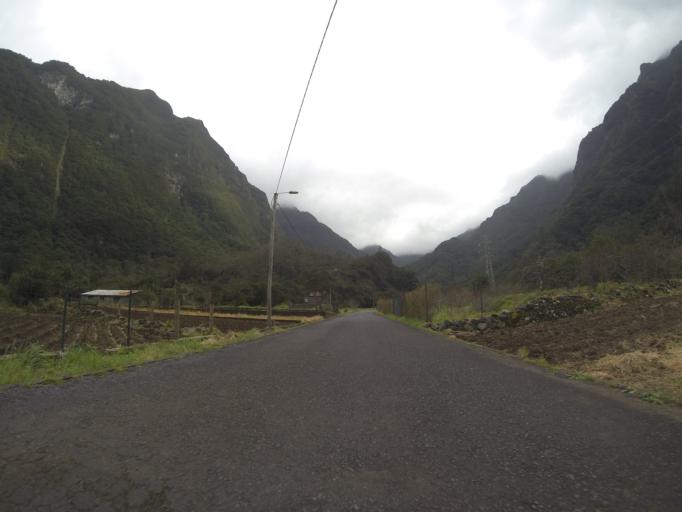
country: PT
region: Madeira
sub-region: Porto Moniz
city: Porto Moniz
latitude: 32.8042
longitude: -17.1153
